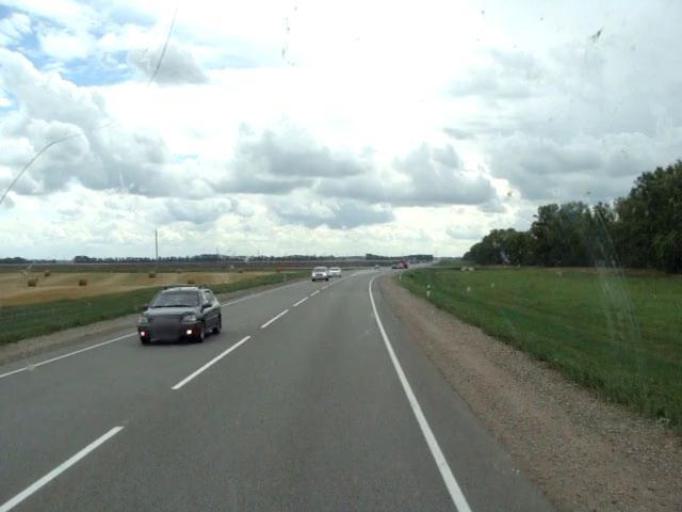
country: RU
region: Altai Krai
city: Shubenka
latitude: 52.6786
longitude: 85.0497
